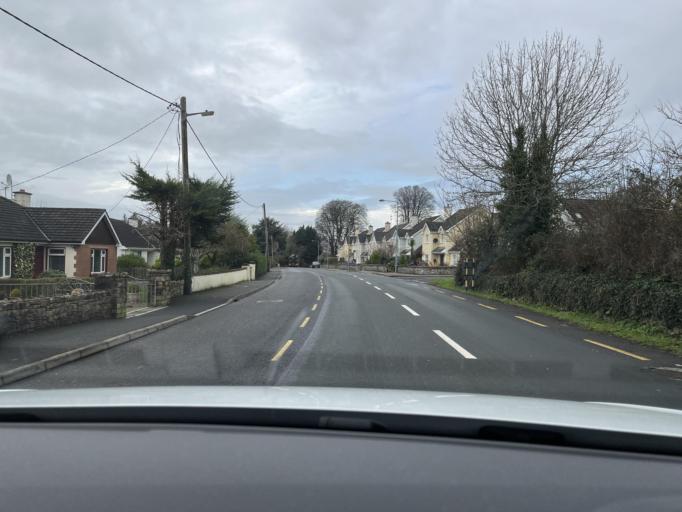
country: IE
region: Connaught
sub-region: County Leitrim
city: Manorhamilton
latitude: 54.2291
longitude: -8.2959
